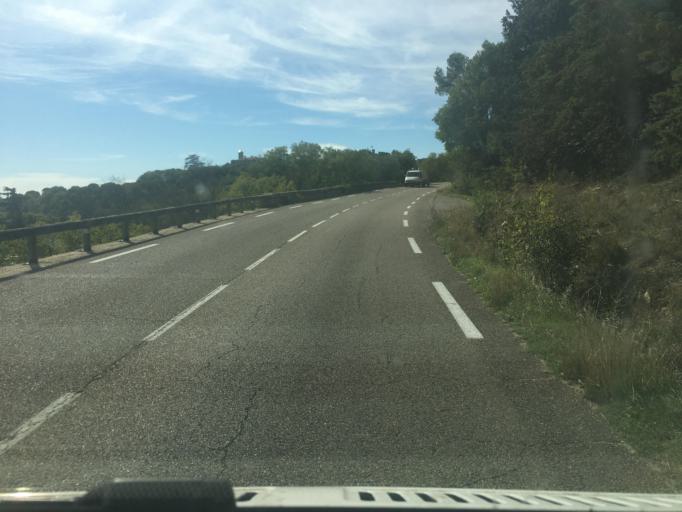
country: FR
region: Languedoc-Roussillon
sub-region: Departement du Gard
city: Uzes
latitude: 44.0155
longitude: 4.4290
